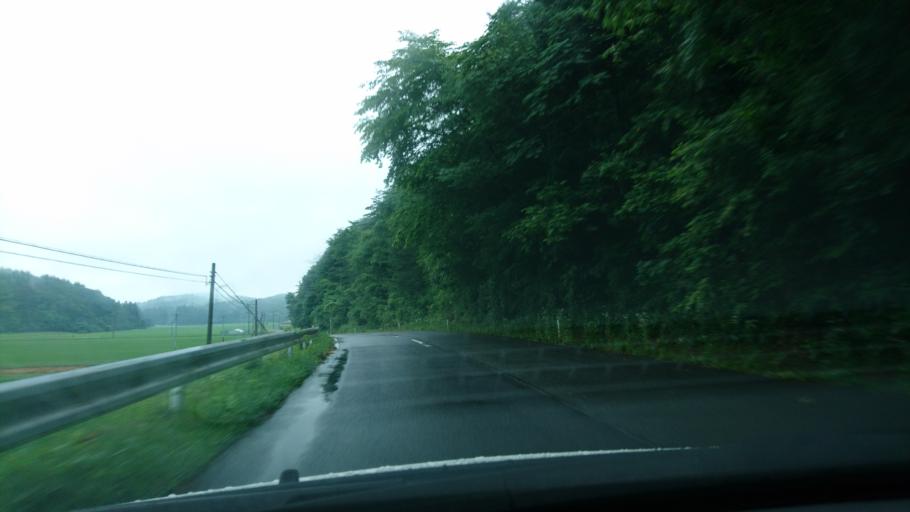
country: JP
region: Iwate
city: Ichinoseki
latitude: 38.8556
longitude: 141.0185
